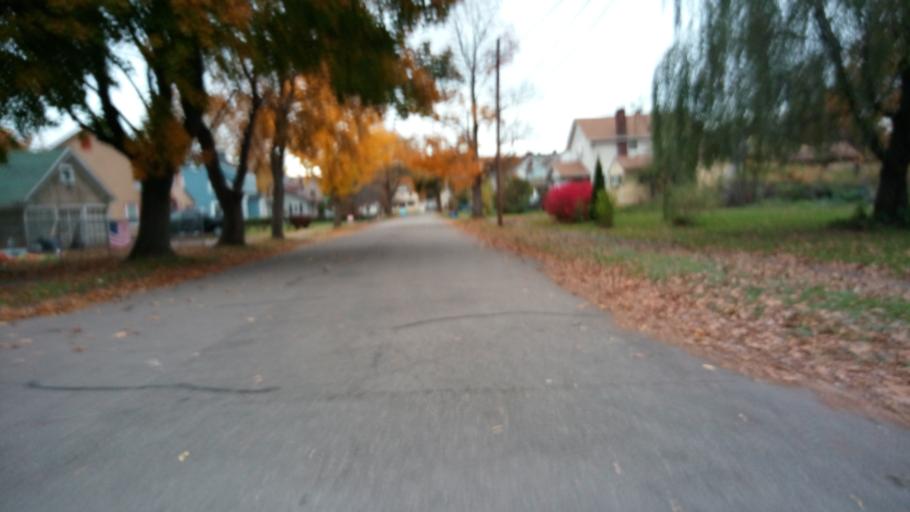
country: US
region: New York
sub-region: Chemung County
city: Elmira
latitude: 42.0791
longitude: -76.7932
